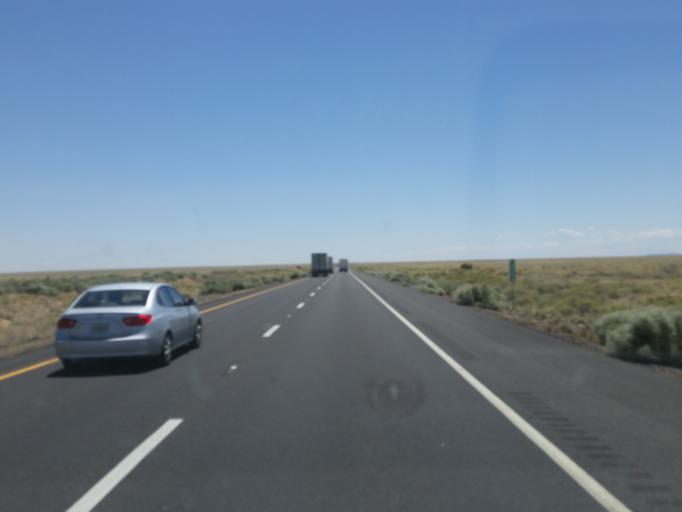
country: US
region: Arizona
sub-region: Coconino County
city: Flagstaff
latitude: 35.1471
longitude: -111.2335
